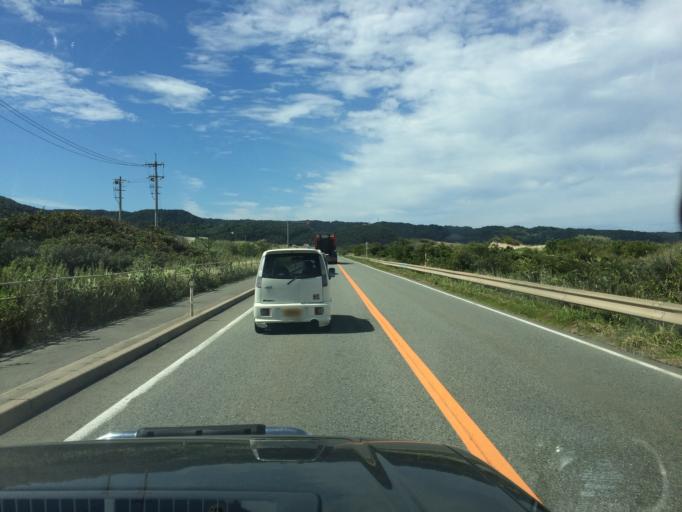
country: JP
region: Tottori
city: Tottori
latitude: 35.5178
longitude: 134.0422
